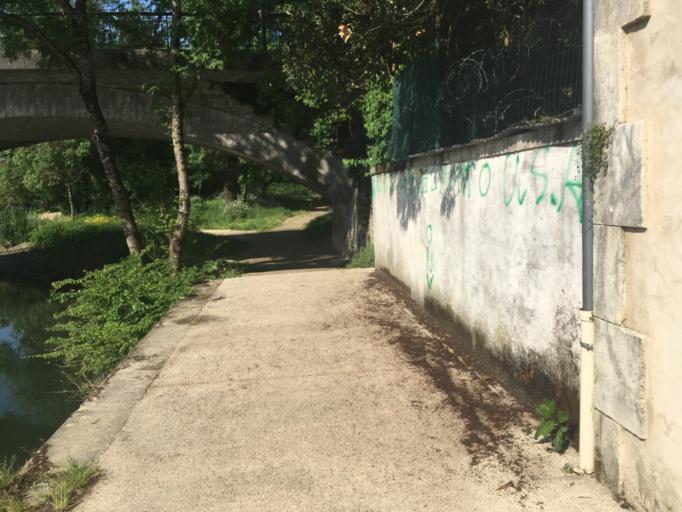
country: FR
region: Poitou-Charentes
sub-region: Departement de la Charente
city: Cognac
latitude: 45.6892
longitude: -0.3391
